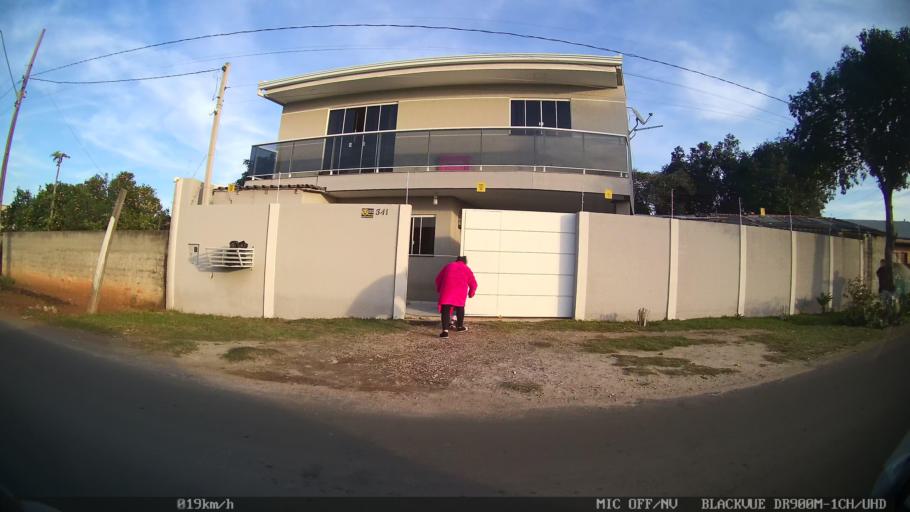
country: BR
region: Parana
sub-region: Pinhais
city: Pinhais
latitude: -25.4389
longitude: -49.1654
